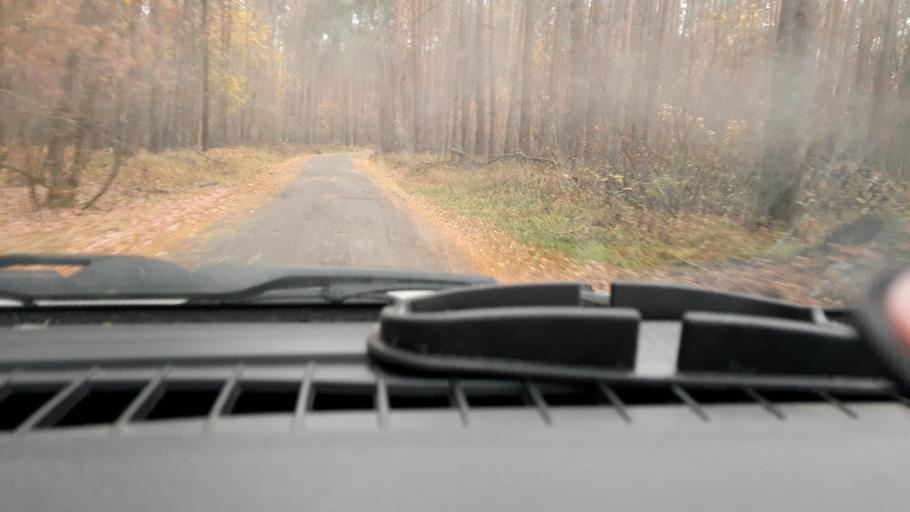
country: RU
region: Nizjnij Novgorod
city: Sitniki
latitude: 56.4197
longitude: 44.0461
